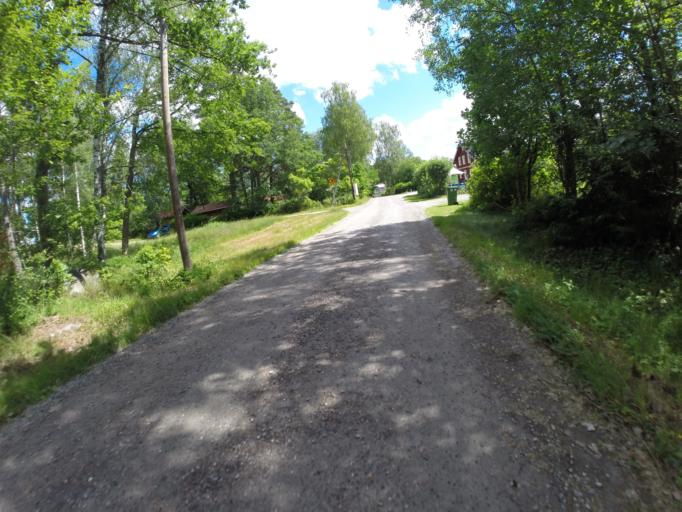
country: SE
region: Soedermanland
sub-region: Eskilstuna Kommun
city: Kvicksund
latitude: 59.4521
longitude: 16.3498
